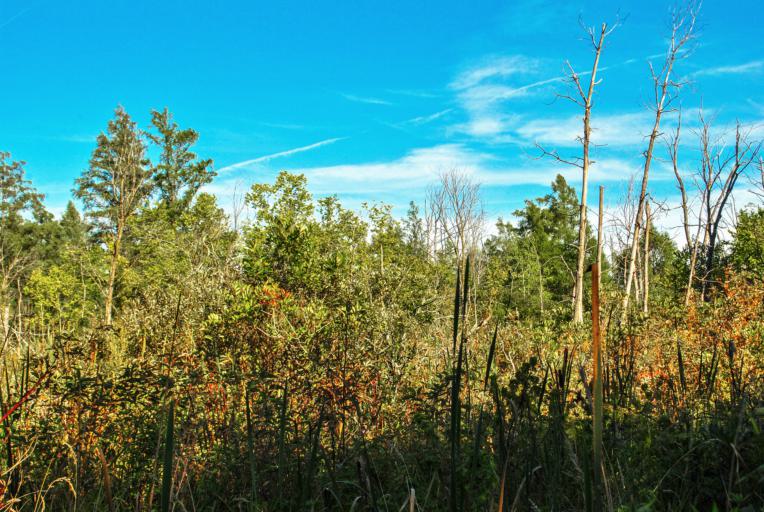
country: US
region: Wisconsin
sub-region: Jefferson County
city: Lake Mills
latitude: 43.0578
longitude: -88.9489
